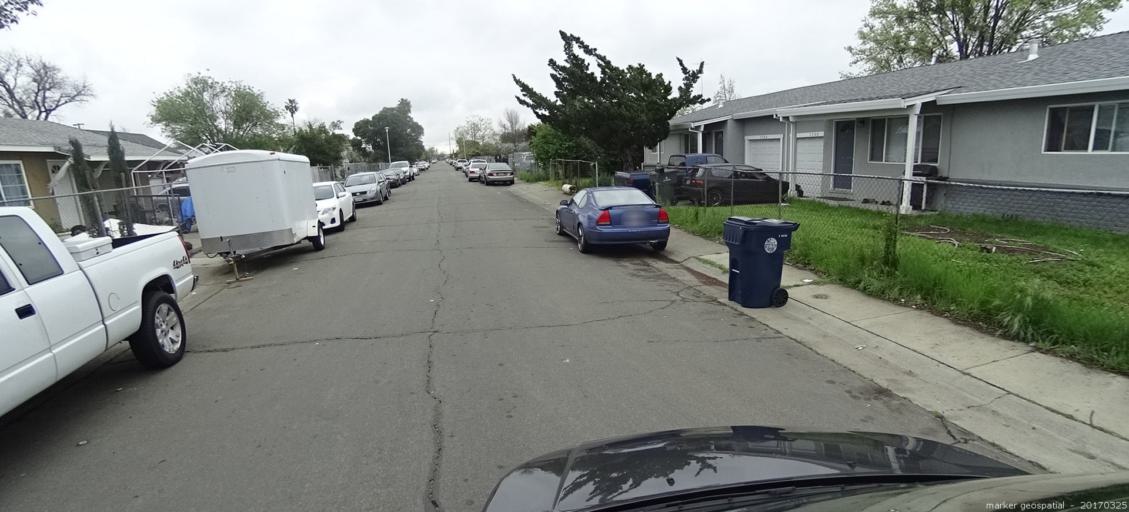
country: US
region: California
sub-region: Sacramento County
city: Florin
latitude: 38.5231
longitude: -121.4144
